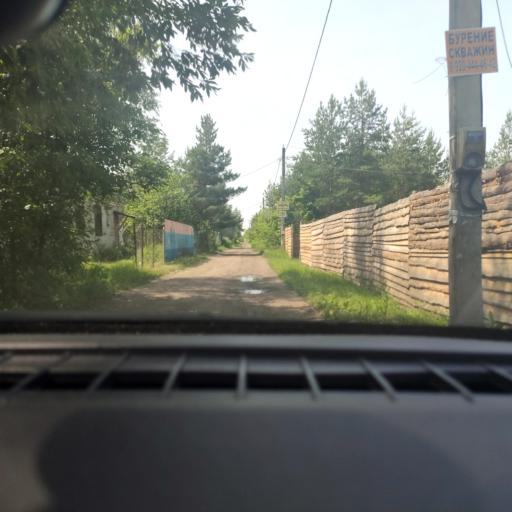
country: RU
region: Voronezj
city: Podgornoye
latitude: 51.8496
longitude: 39.2103
